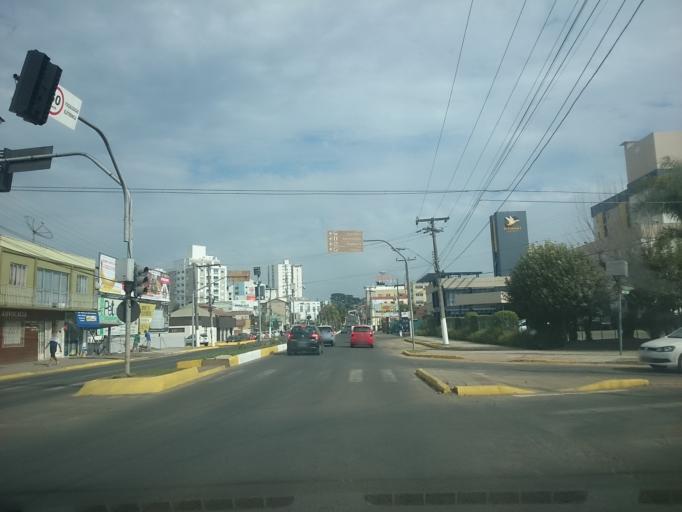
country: BR
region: Santa Catarina
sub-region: Lages
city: Lages
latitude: -27.8109
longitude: -50.3178
